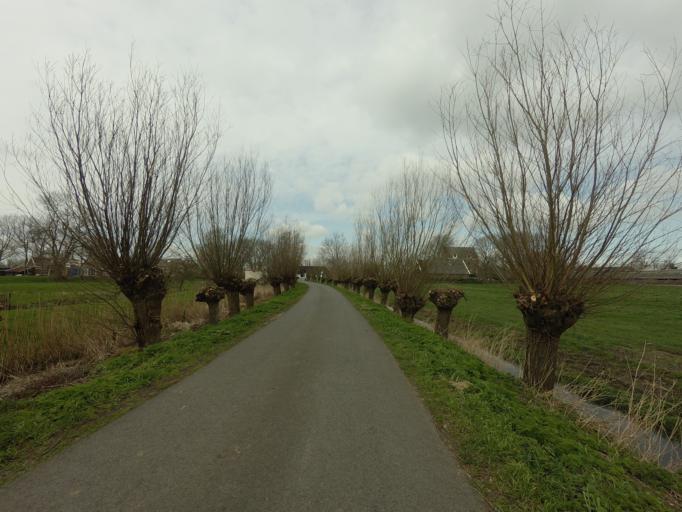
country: NL
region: North Holland
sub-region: Gemeente Amsterdam
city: Driemond
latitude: 52.2787
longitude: 5.0054
